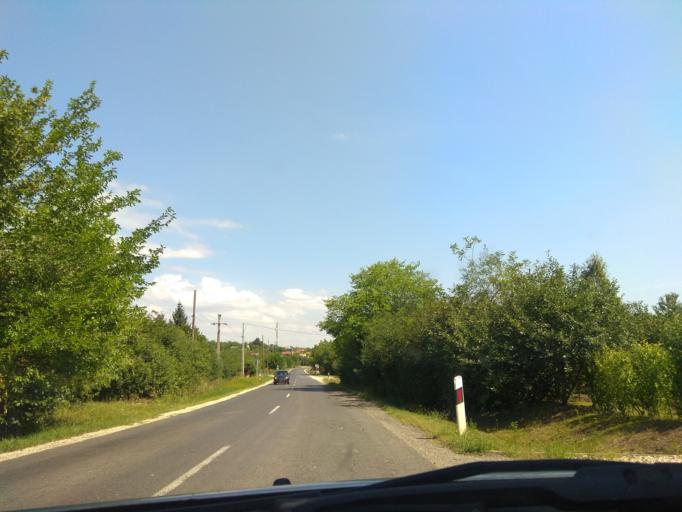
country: HU
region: Borsod-Abauj-Zemplen
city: Malyi
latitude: 48.0340
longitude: 20.7725
